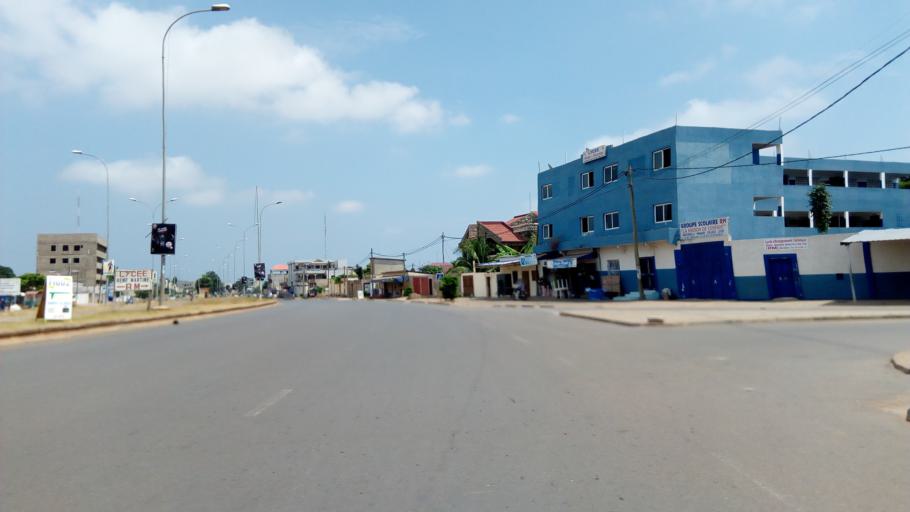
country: TG
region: Maritime
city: Lome
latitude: 6.2107
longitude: 1.1883
